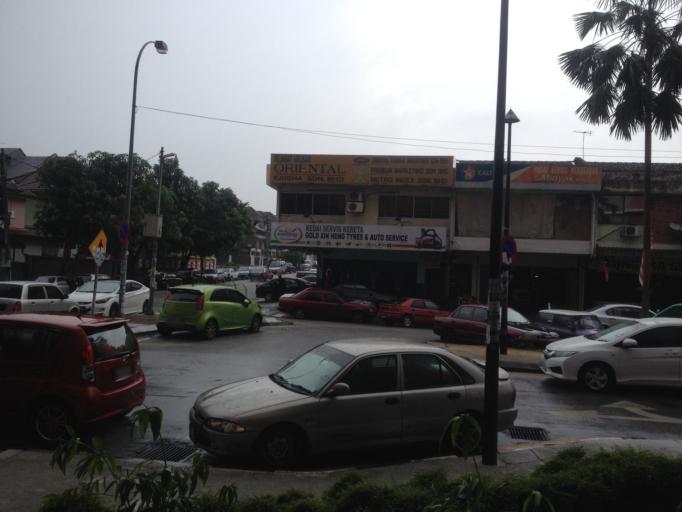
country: MY
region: Kuala Lumpur
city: Kuala Lumpur
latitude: 3.0915
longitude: 101.7128
